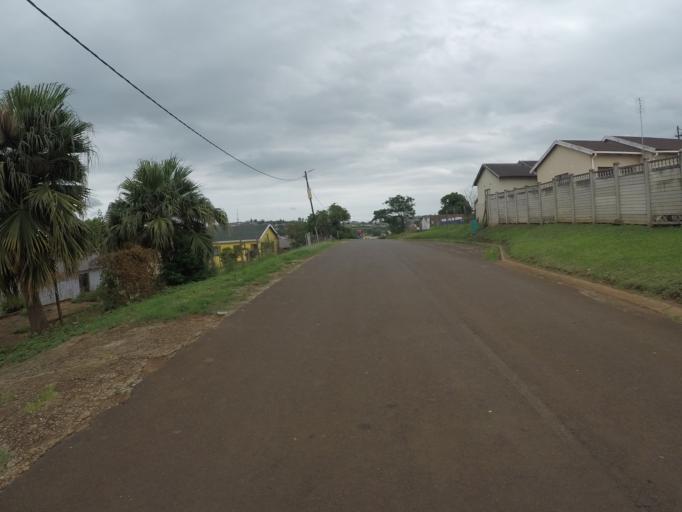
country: ZA
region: KwaZulu-Natal
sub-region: uThungulu District Municipality
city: Empangeni
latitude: -28.7740
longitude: 31.8581
